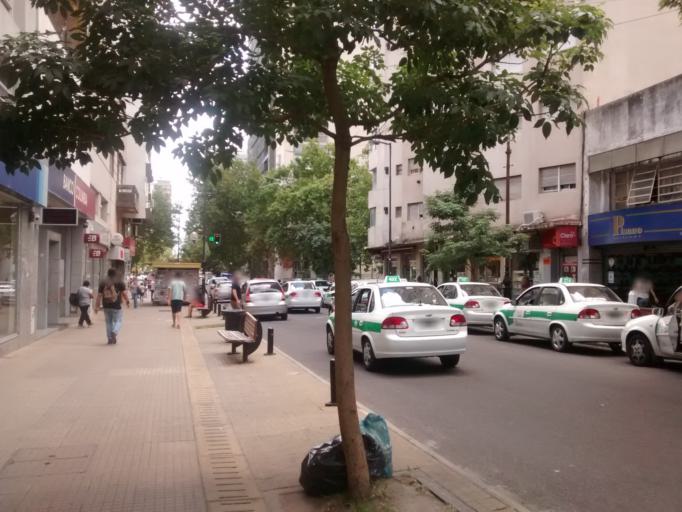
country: AR
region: Buenos Aires
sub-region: Partido de La Plata
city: La Plata
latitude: -34.9219
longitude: -57.9518
